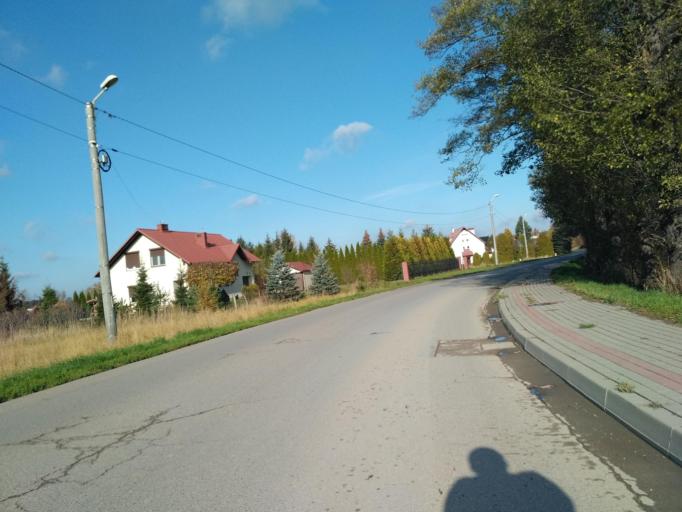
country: PL
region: Subcarpathian Voivodeship
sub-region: Powiat rzeszowski
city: Niechobrz
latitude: 50.0135
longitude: 21.8956
